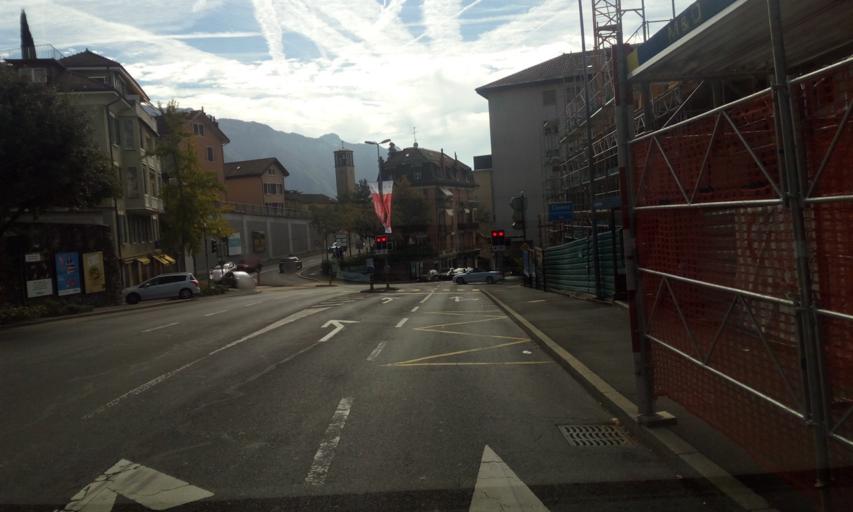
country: CH
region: Vaud
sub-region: Riviera-Pays-d'Enhaut District
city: Le Chatelard
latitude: 46.4448
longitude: 6.8961
